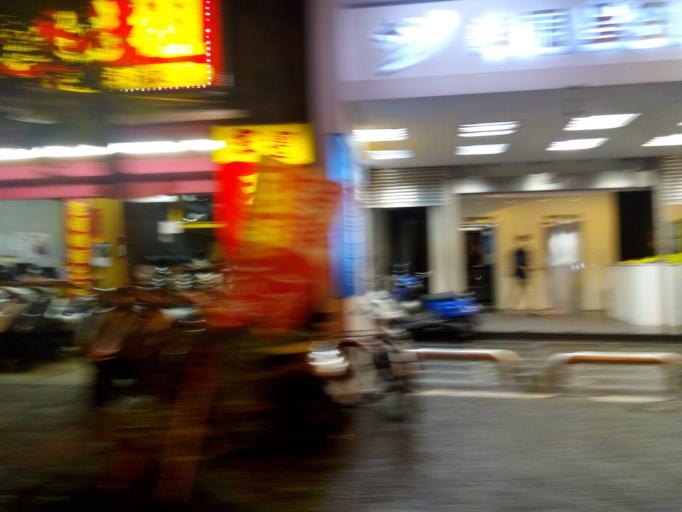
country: TW
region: Taiwan
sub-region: Yilan
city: Yilan
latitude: 24.6778
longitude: 121.7740
